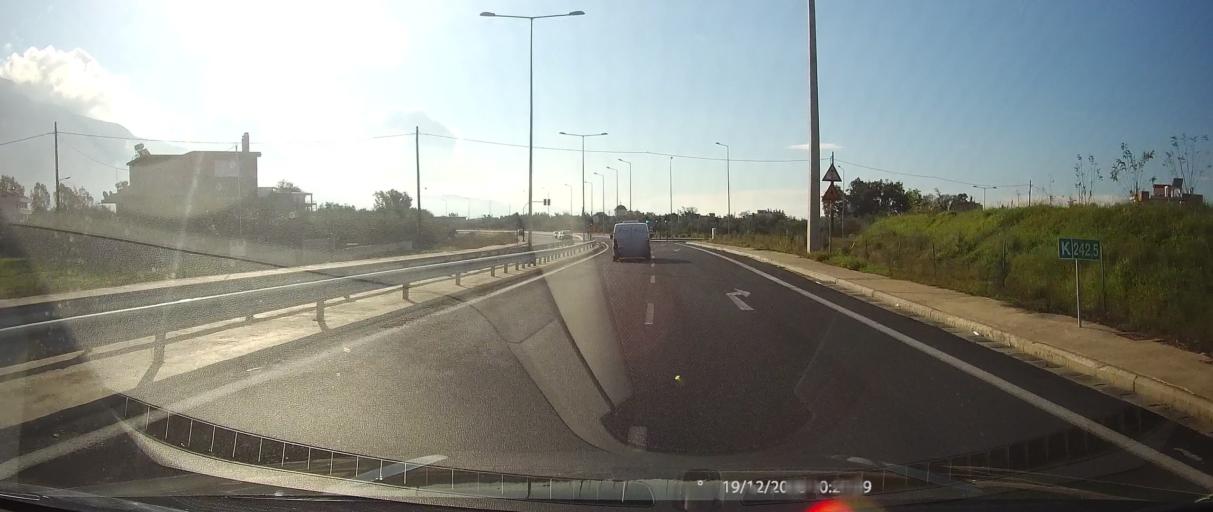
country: GR
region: Peloponnese
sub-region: Nomos Messinias
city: Kalamata
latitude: 37.0341
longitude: 22.1355
